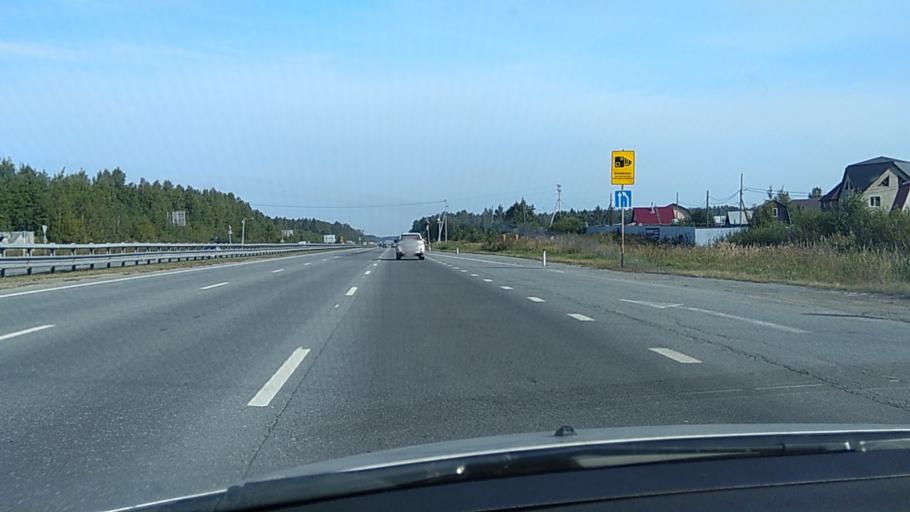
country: RU
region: Sverdlovsk
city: Shuvakish
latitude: 56.9402
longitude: 60.5123
